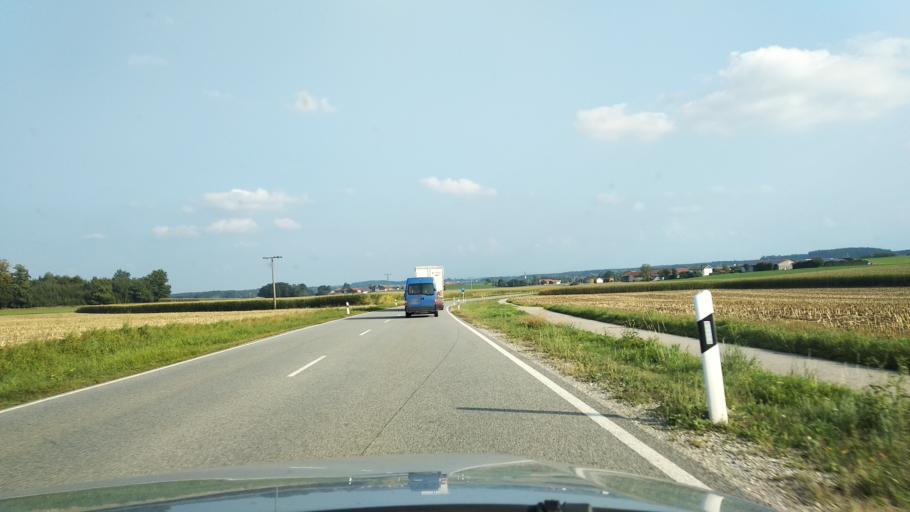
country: DE
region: Bavaria
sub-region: Upper Bavaria
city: Obing
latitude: 48.0210
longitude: 12.3781
